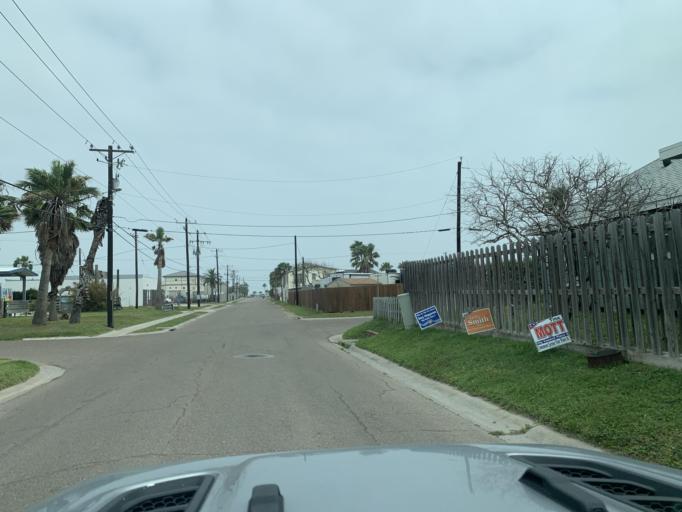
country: US
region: Texas
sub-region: Nueces County
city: Port Aransas
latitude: 27.8365
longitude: -97.0591
